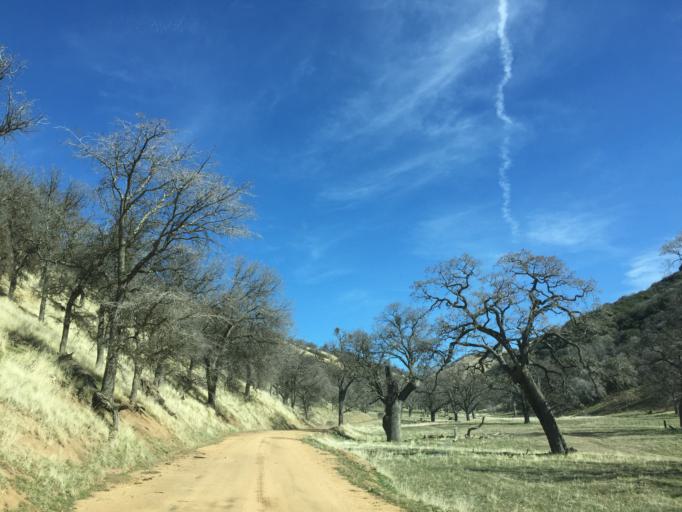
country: US
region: California
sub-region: Kern County
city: Lebec
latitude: 34.9068
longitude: -118.7119
